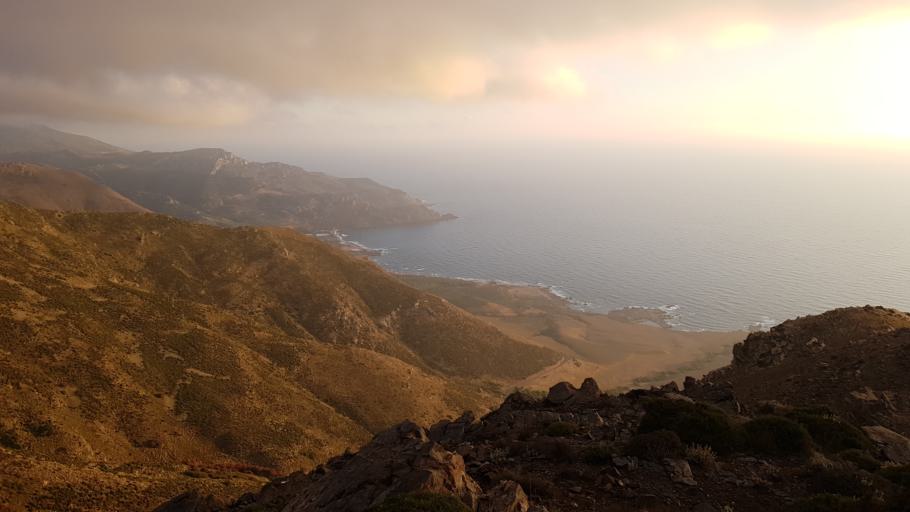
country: GR
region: Crete
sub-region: Nomos Chanias
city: Vryses
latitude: 35.4440
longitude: 23.5895
